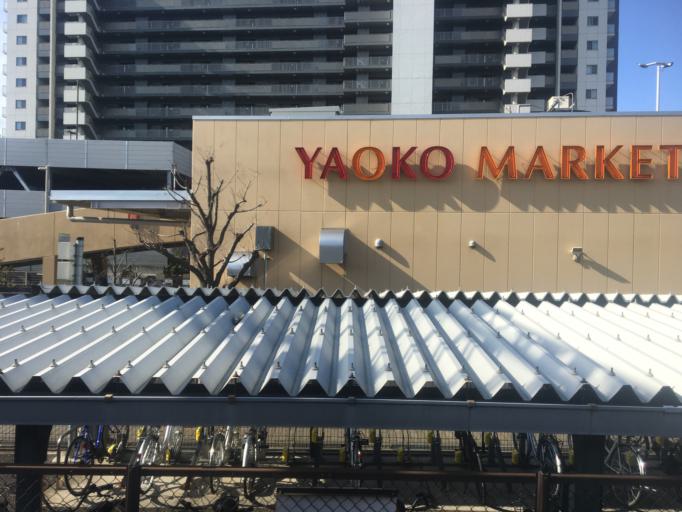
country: JP
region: Saitama
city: Sakado
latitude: 35.9484
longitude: 139.4093
